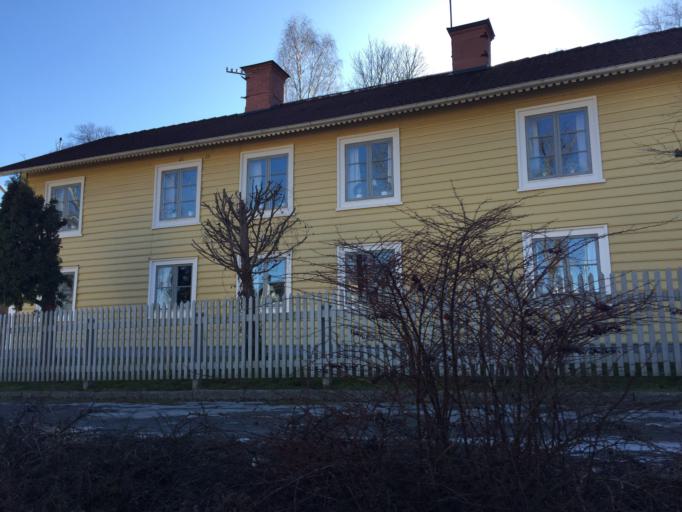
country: SE
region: OEstergoetland
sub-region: Finspangs Kommun
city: Finspang
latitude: 58.7094
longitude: 15.7695
